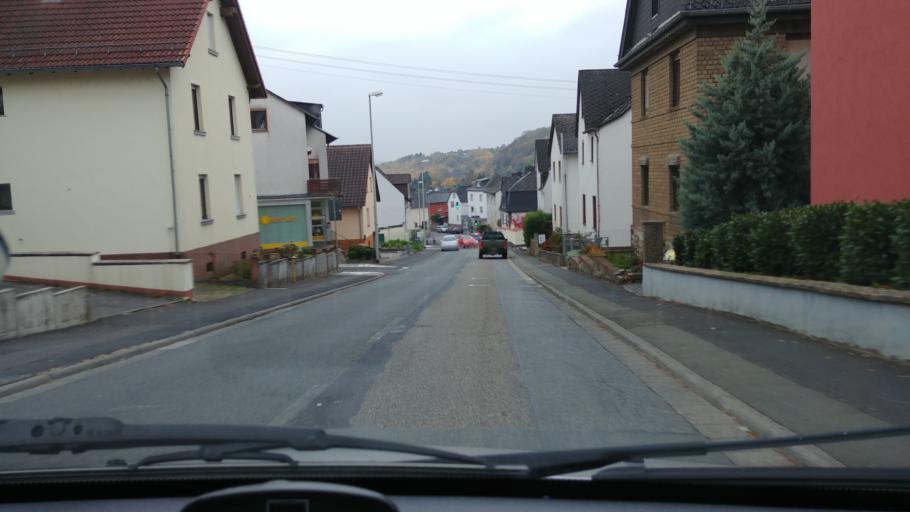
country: DE
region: Hesse
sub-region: Regierungsbezirk Giessen
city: Dehrn
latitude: 50.4212
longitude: 8.0978
